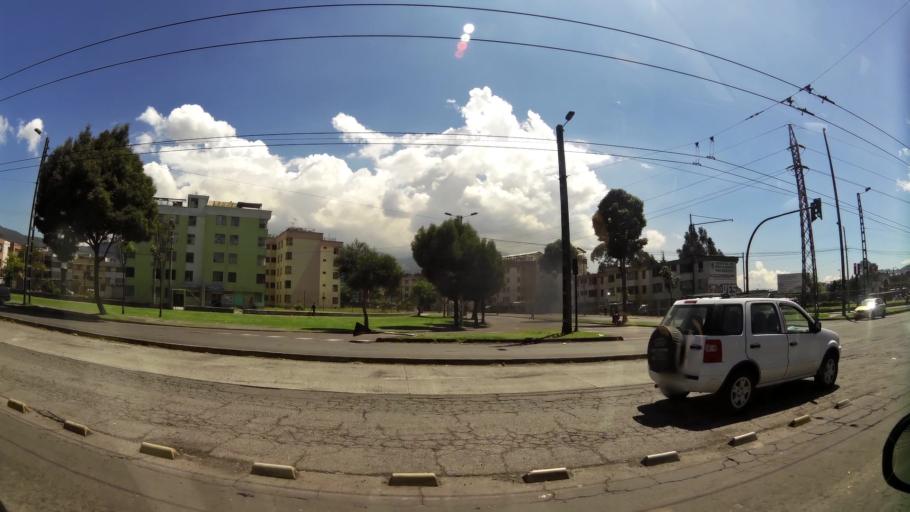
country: EC
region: Pichincha
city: Quito
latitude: -0.2689
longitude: -78.5334
